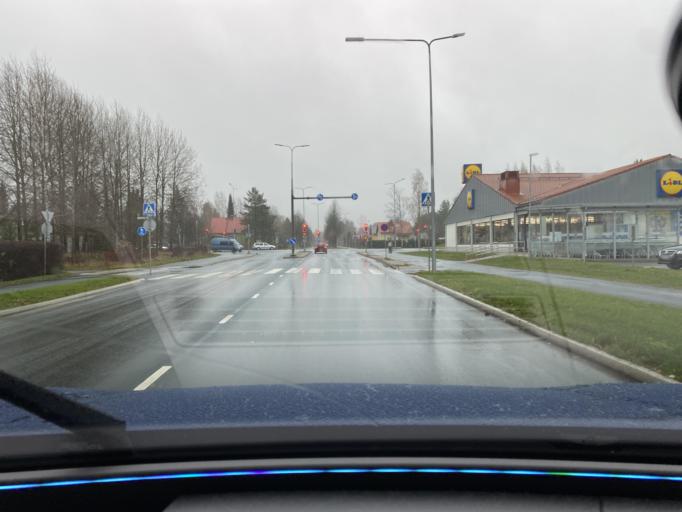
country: FI
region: Haeme
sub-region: Forssa
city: Forssa
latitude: 60.8080
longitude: 23.6212
